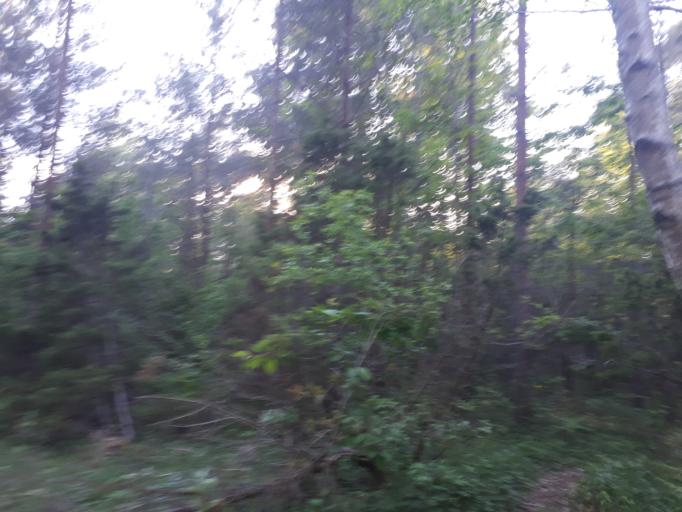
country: SE
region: Gotland
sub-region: Gotland
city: Visby
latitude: 57.6040
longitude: 18.2892
